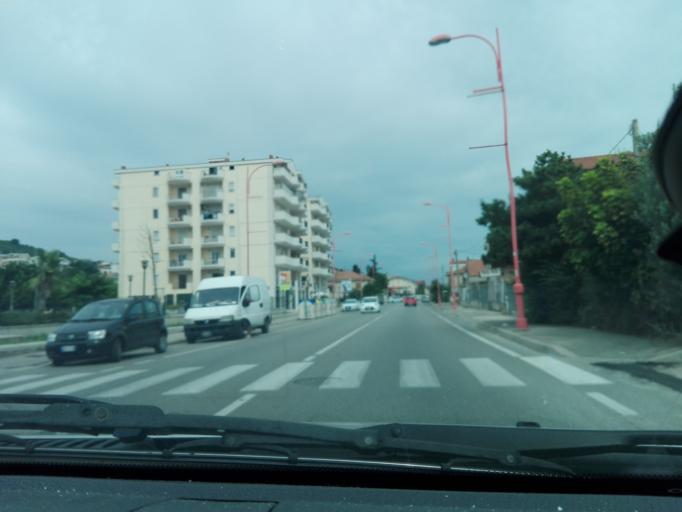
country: IT
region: Abruzzo
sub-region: Provincia di Pescara
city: Montesilvano Marina
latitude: 42.4966
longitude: 14.1704
